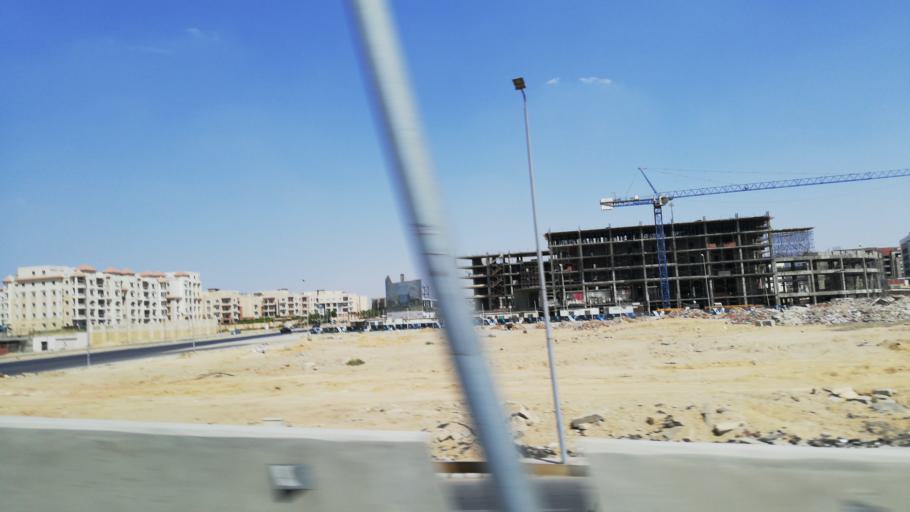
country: EG
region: Muhafazat al Qalyubiyah
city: Al Khankah
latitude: 30.0278
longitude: 31.4751
